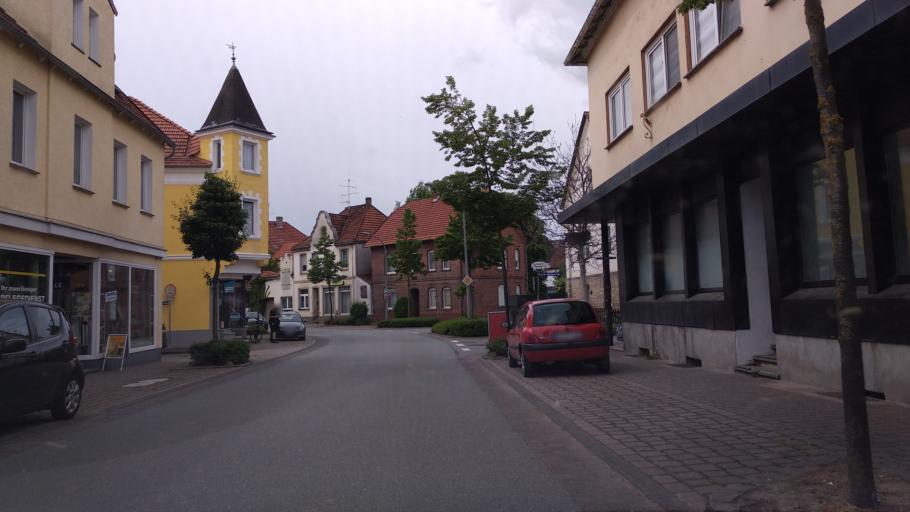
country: DE
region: North Rhine-Westphalia
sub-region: Regierungsbezirk Detmold
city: Willebadessen
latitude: 51.5990
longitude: 9.1289
